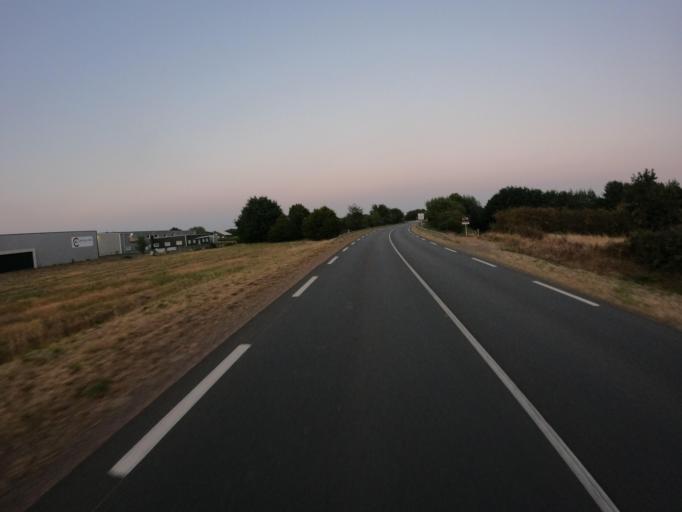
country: FR
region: Pays de la Loire
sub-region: Departement de Maine-et-Loire
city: Cande
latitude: 47.5695
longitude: -1.0287
